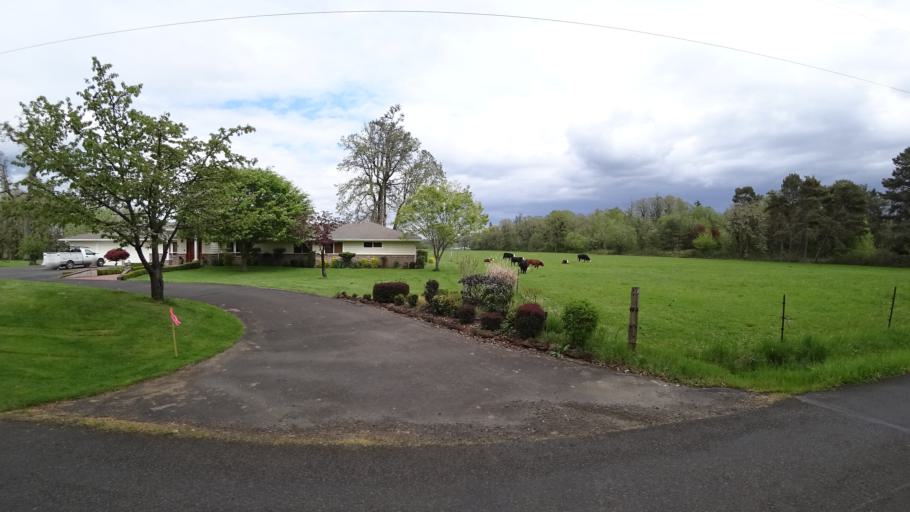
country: US
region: Oregon
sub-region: Washington County
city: Hillsboro
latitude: 45.5591
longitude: -122.9527
